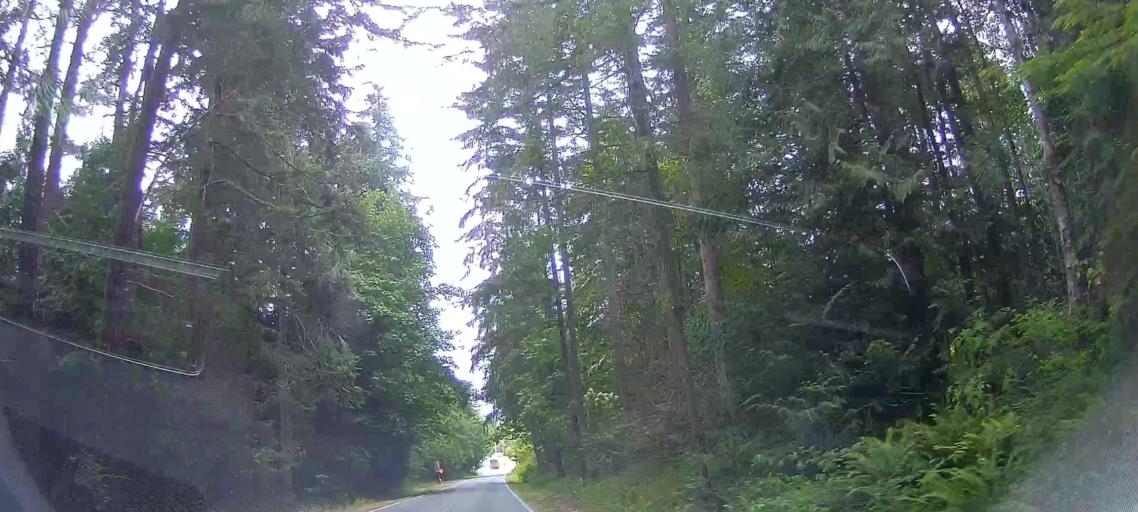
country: US
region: Washington
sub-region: Skagit County
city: Anacortes
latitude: 48.4827
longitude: -122.6255
